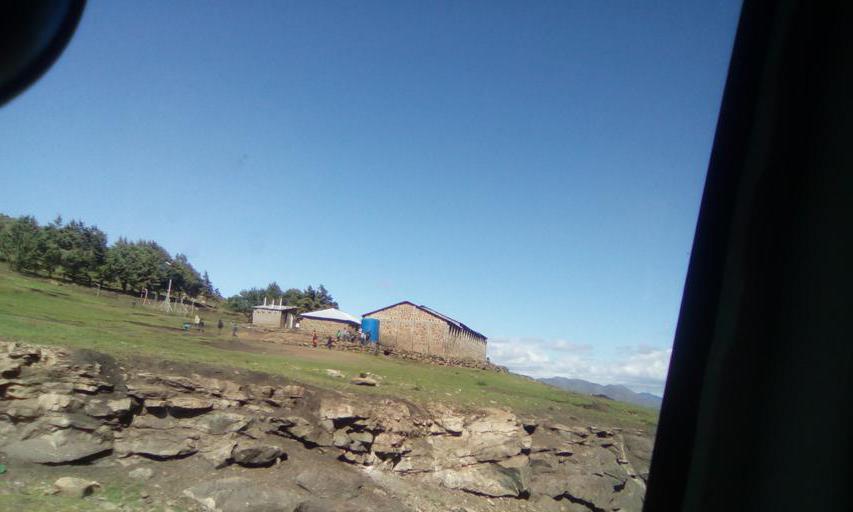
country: LS
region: Maseru
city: Nako
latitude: -29.8926
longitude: 28.1251
